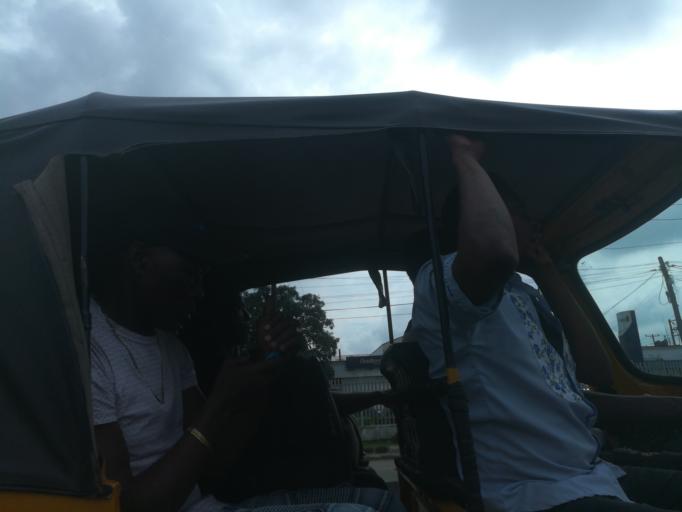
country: NG
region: Lagos
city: Ikeja
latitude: 6.6052
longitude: 3.3368
